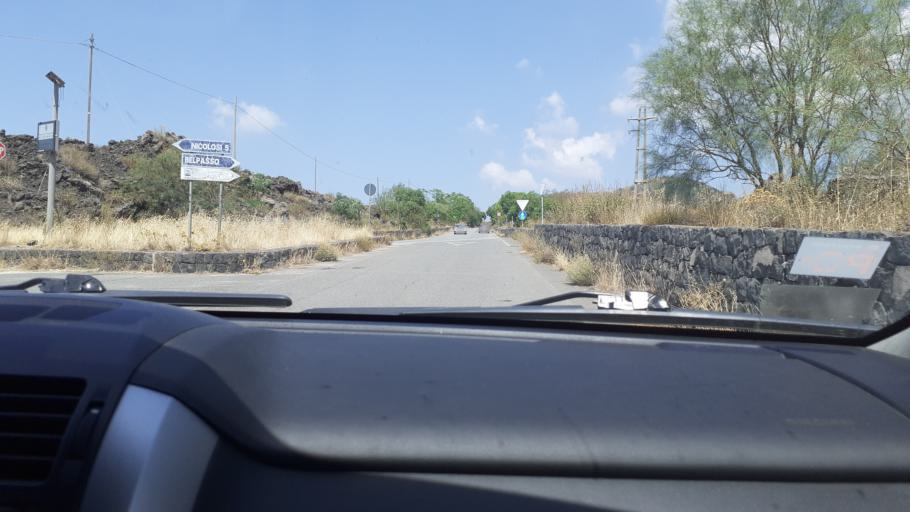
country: IT
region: Sicily
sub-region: Catania
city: Nicolosi
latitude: 37.6456
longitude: 14.9946
